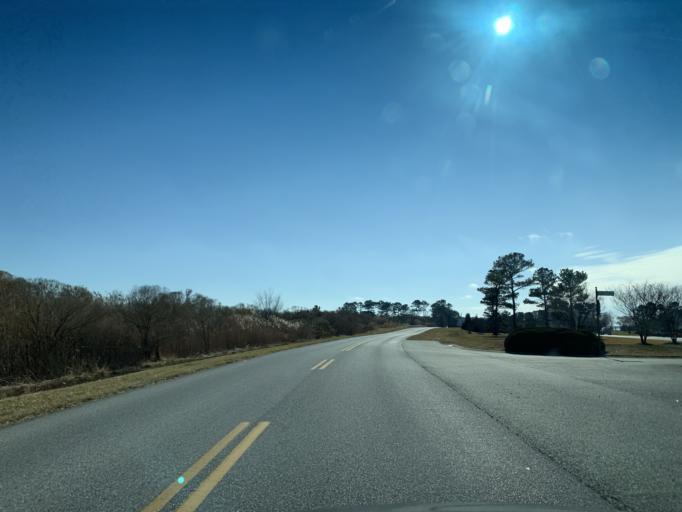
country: US
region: Maryland
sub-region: Worcester County
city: Ocean Pines
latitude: 38.4084
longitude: -75.1090
